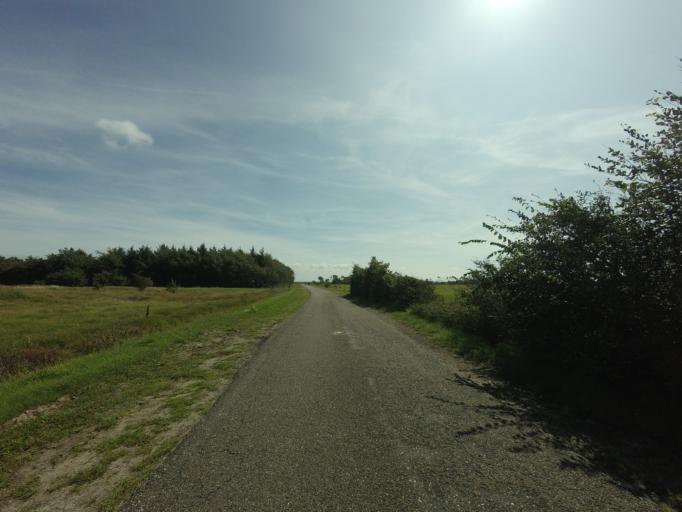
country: NL
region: Friesland
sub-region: Gemeente Ameland
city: Hollum
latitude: 53.4437
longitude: 5.6625
